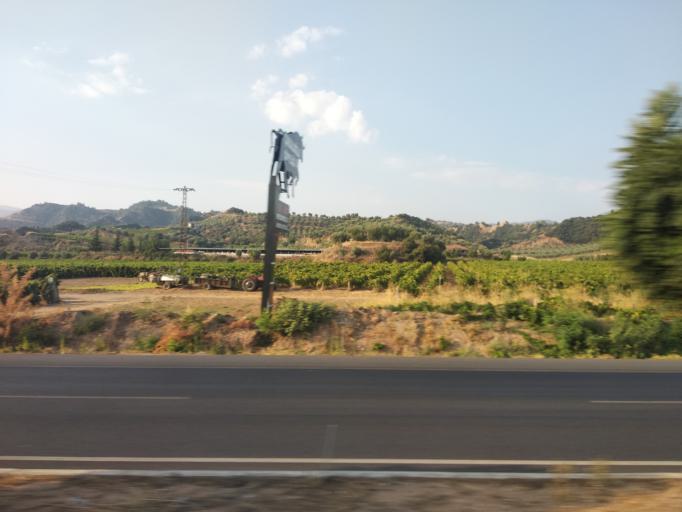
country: TR
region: Manisa
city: Ahmetli
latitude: 38.5082
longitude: 27.9864
